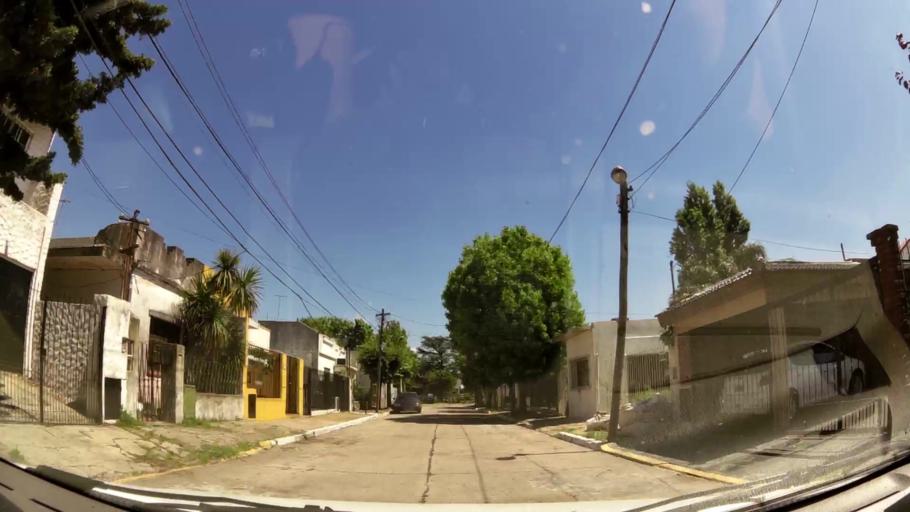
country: AR
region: Buenos Aires
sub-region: Partido de Merlo
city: Merlo
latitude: -34.6755
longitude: -58.6897
